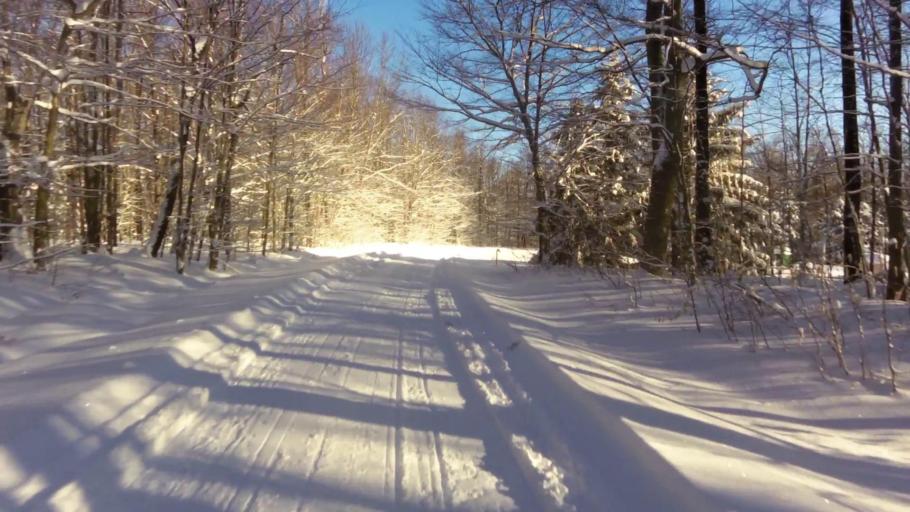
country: US
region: New York
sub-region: Chautauqua County
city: Falconer
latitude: 42.2492
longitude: -79.2127
